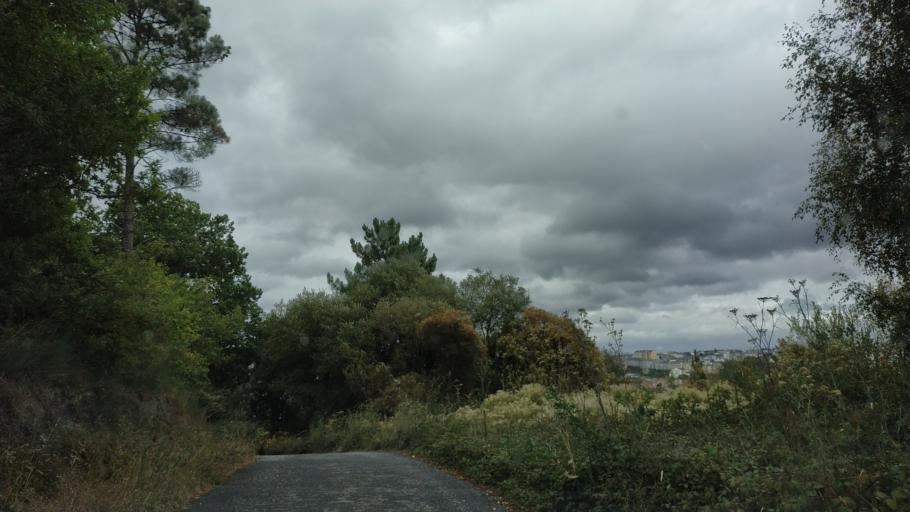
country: ES
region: Galicia
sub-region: Provincia de Lugo
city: Lugo
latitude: 42.9982
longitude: -7.5752
